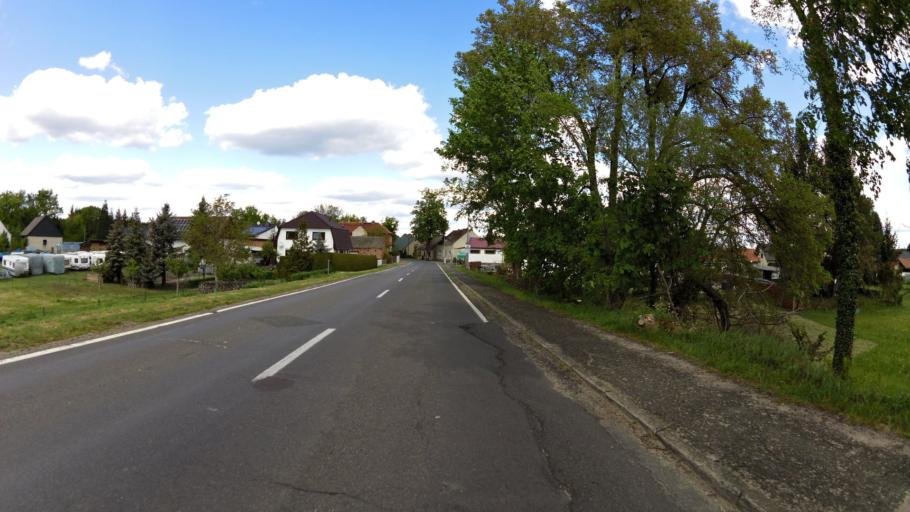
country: DE
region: Brandenburg
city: Schlepzig
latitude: 52.1187
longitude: 13.9501
